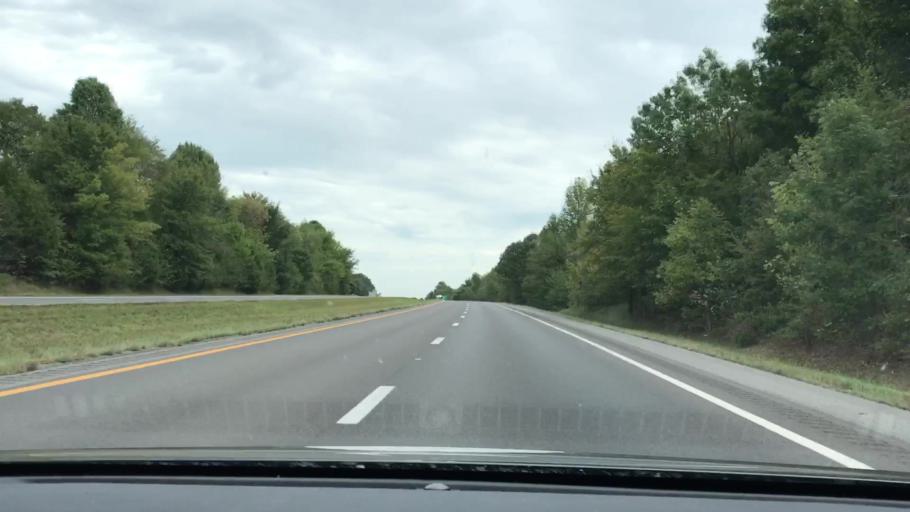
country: US
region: Kentucky
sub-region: Graves County
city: Mayfield
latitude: 36.7710
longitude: -88.6086
